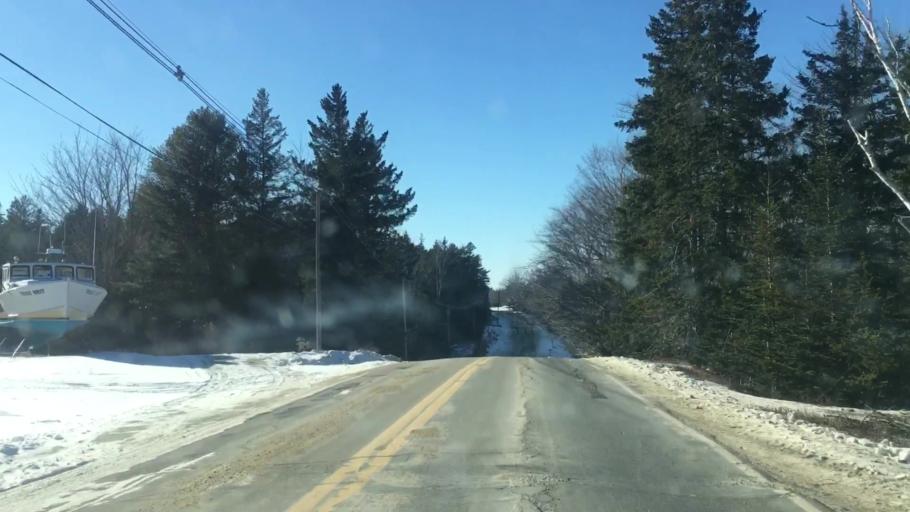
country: US
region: Maine
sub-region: Hancock County
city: Castine
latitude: 44.3408
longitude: -68.7250
